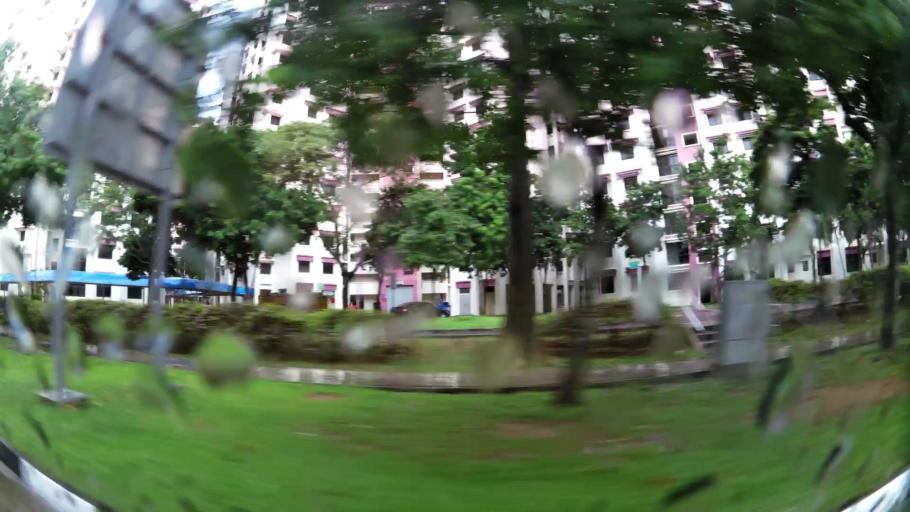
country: MY
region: Johor
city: Kampung Pasir Gudang Baru
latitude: 1.3865
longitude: 103.8951
